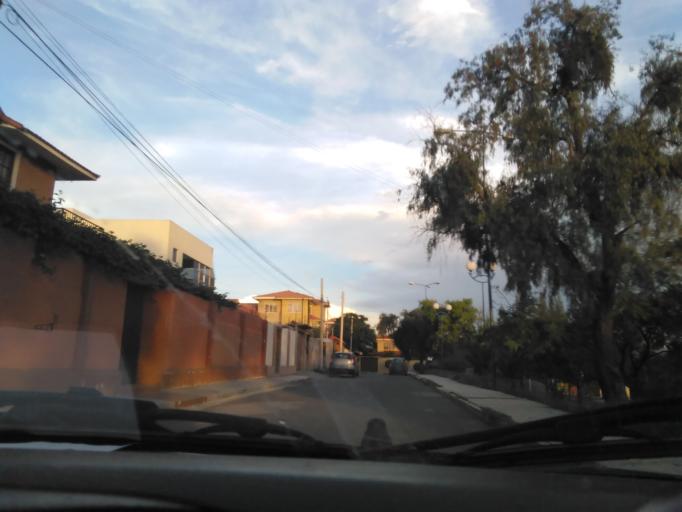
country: BO
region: Cochabamba
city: Cochabamba
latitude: -17.3726
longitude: -66.1386
